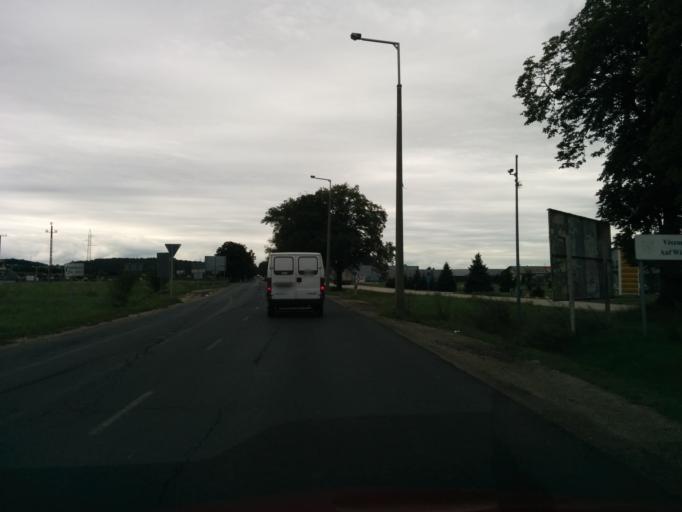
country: HU
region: Gyor-Moson-Sopron
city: Sopron
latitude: 47.6689
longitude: 16.6181
